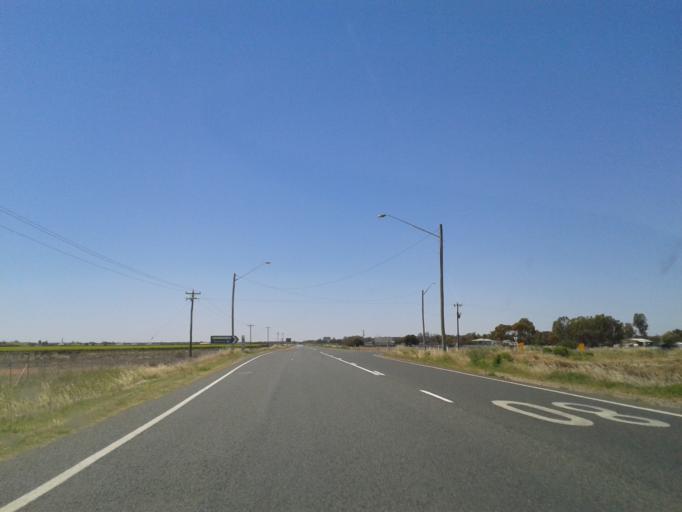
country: AU
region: New South Wales
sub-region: Wentworth
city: Gol Gol
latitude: -34.5581
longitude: 142.7564
